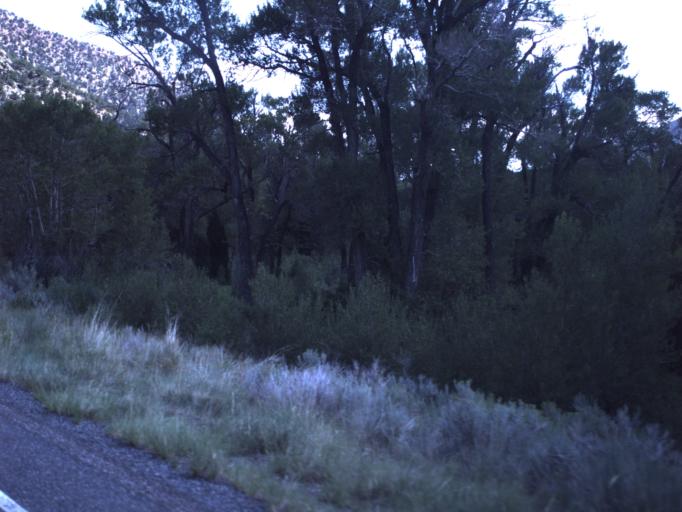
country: US
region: Utah
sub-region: Emery County
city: Huntington
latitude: 39.4047
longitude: -111.1133
